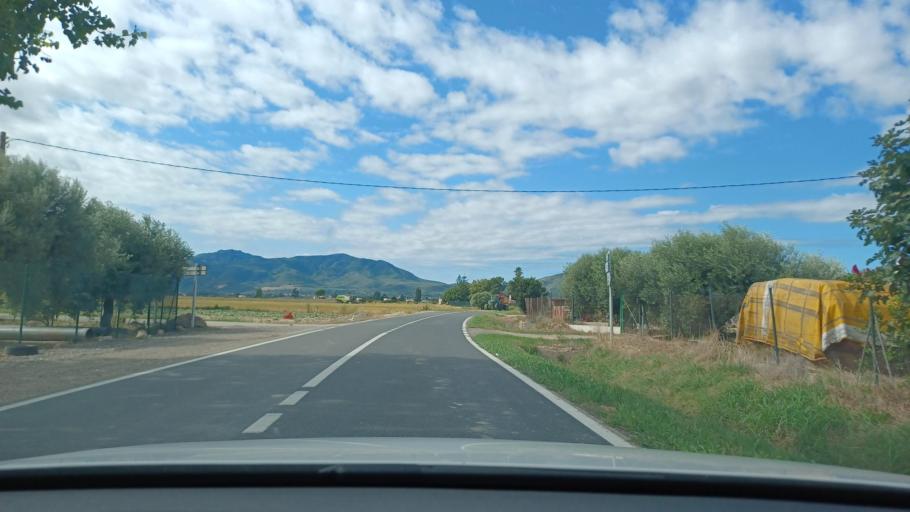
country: ES
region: Catalonia
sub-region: Provincia de Tarragona
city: Amposta
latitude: 40.7032
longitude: 0.6178
